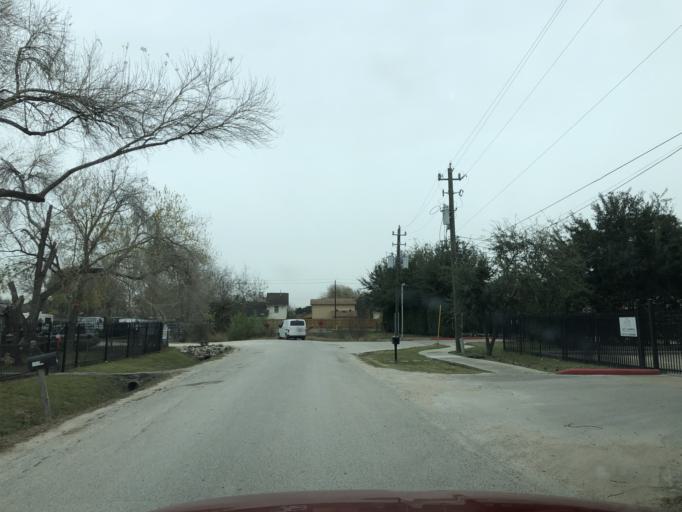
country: US
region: Texas
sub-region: Fort Bend County
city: Missouri City
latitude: 29.6372
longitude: -95.5225
